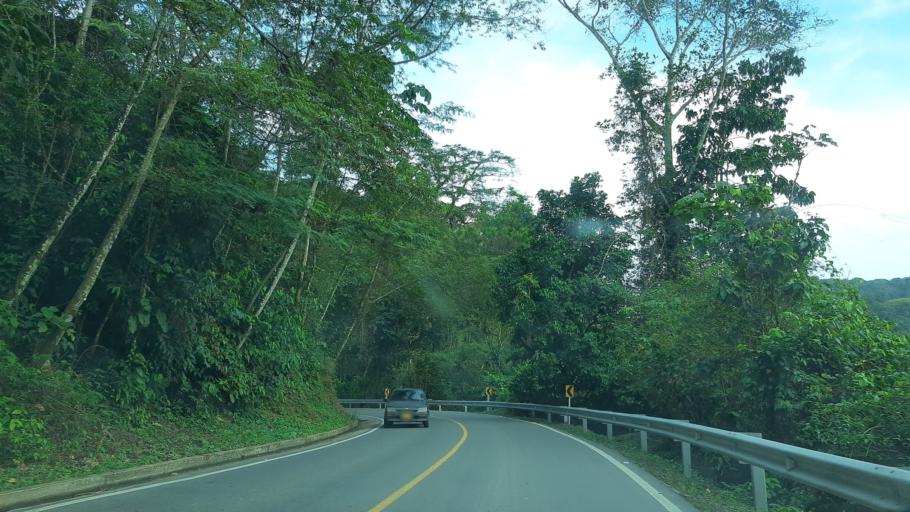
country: CO
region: Boyaca
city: San Luis de Gaceno
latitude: 4.8403
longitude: -73.2155
